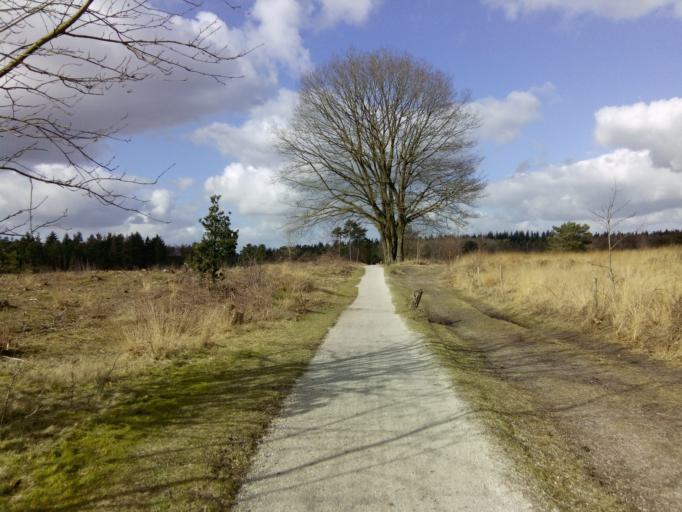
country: NL
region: Utrecht
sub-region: Gemeente Amersfoort
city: Randenbroek
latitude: 52.1206
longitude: 5.3840
